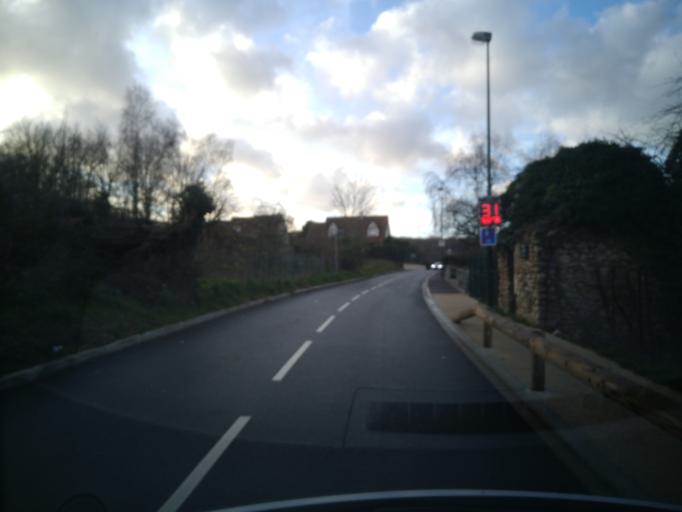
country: FR
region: Ile-de-France
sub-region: Departement des Yvelines
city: Chambourcy
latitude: 48.9008
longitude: 2.0260
